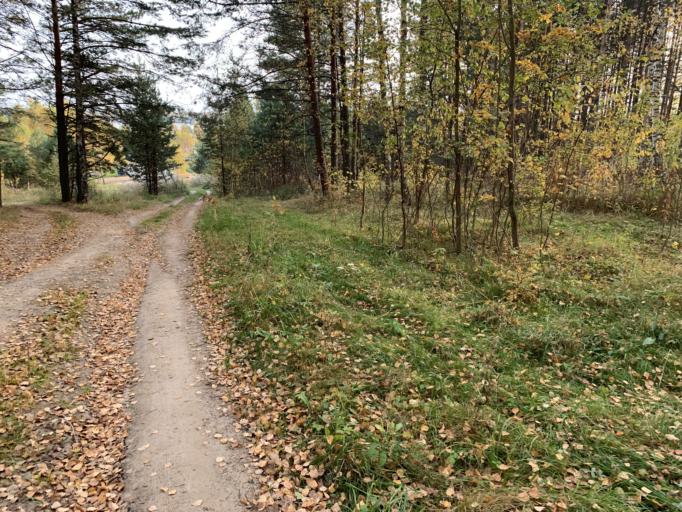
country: RU
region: Jaroslavl
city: Petrovsk
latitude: 56.9825
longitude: 39.3753
